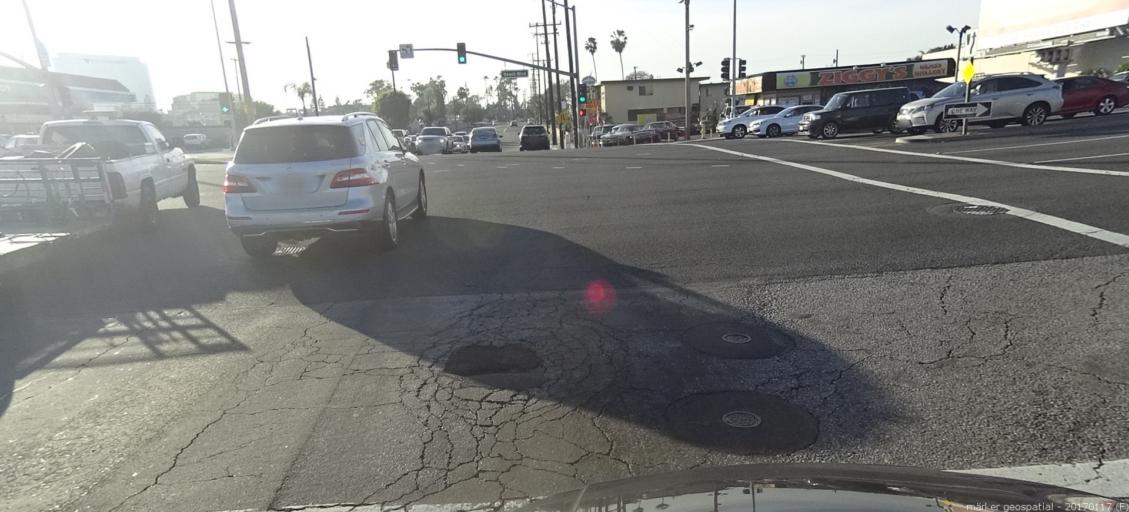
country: US
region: California
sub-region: Orange County
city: Midway City
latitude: 33.7375
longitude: -117.9891
